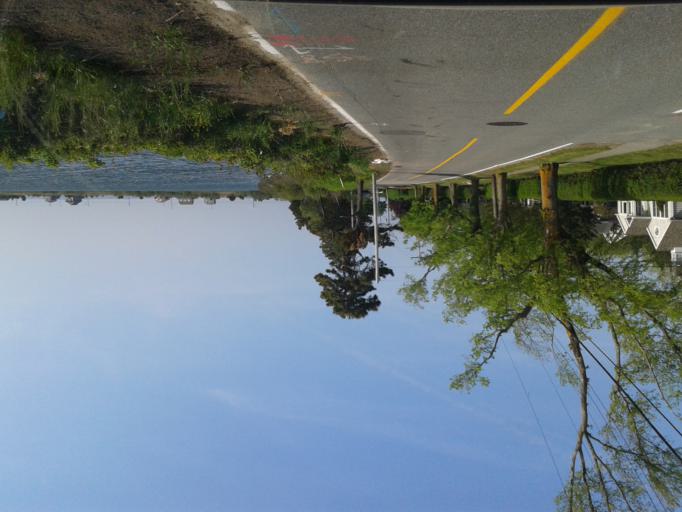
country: US
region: Massachusetts
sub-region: Barnstable County
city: Falmouth
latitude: 41.5455
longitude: -70.6255
